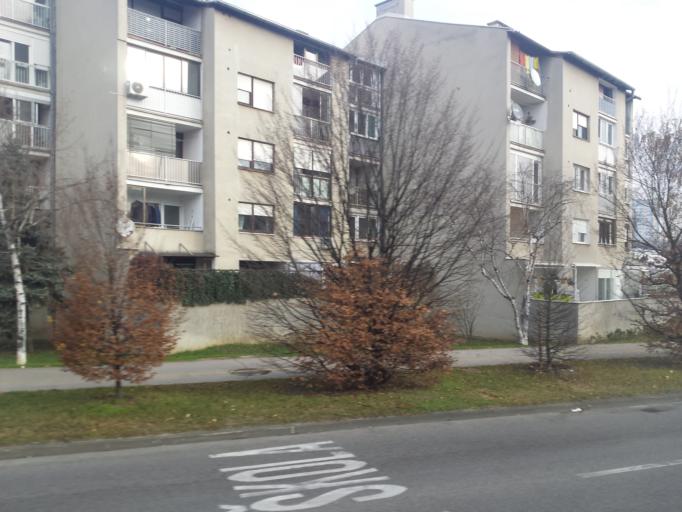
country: HR
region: Grad Zagreb
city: Jankomir
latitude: 45.7875
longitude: 15.9312
